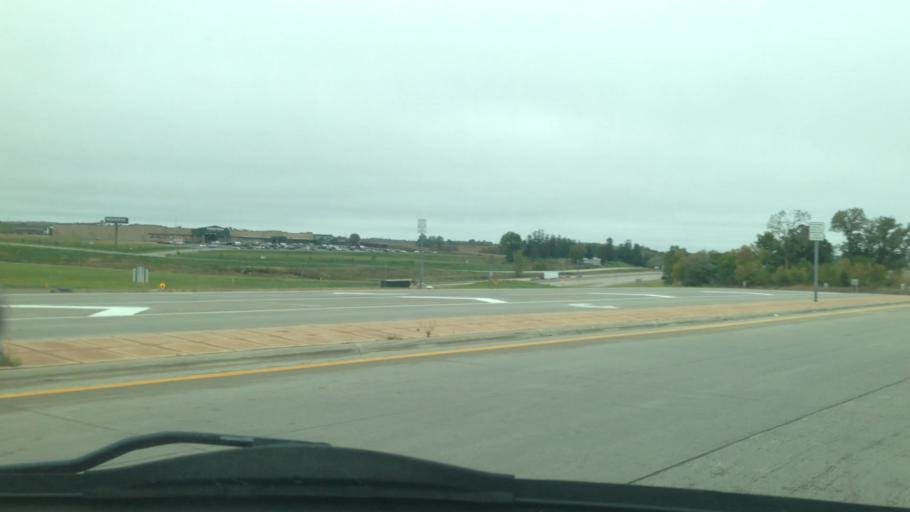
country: US
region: Minnesota
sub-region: Olmsted County
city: Oronoco
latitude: 44.0942
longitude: -92.5095
